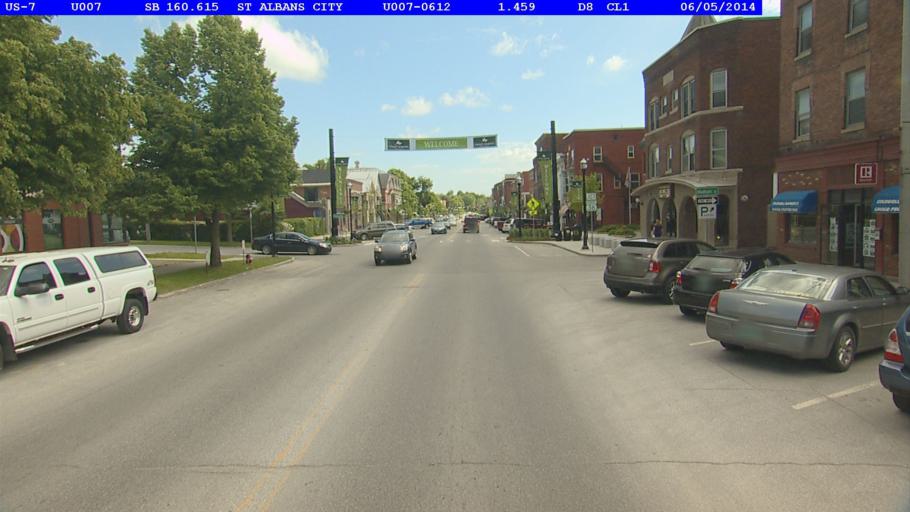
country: US
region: Vermont
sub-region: Franklin County
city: Saint Albans
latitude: 44.8138
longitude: -73.0829
